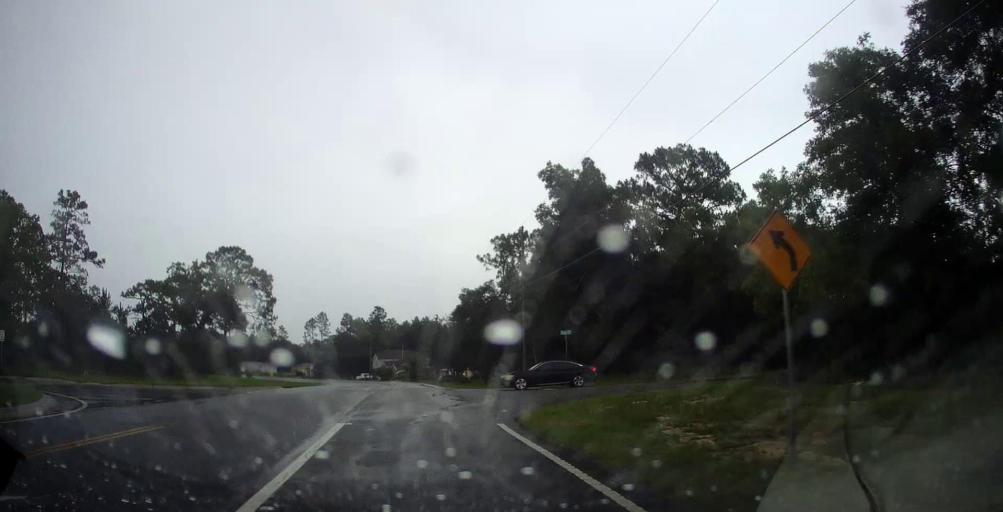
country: US
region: Florida
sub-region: Marion County
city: Silver Springs Shores
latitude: 29.1130
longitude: -82.0196
